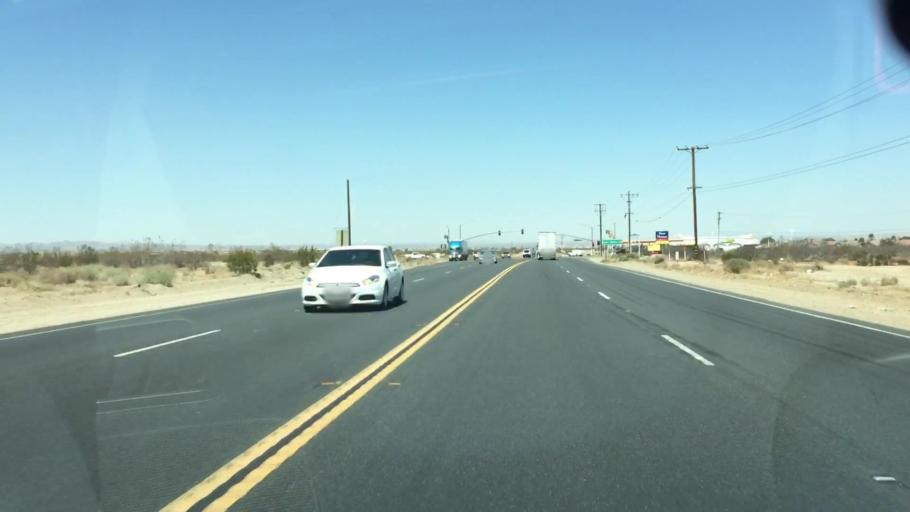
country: US
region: California
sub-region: San Bernardino County
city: Mountain View Acres
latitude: 34.4680
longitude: -117.3995
